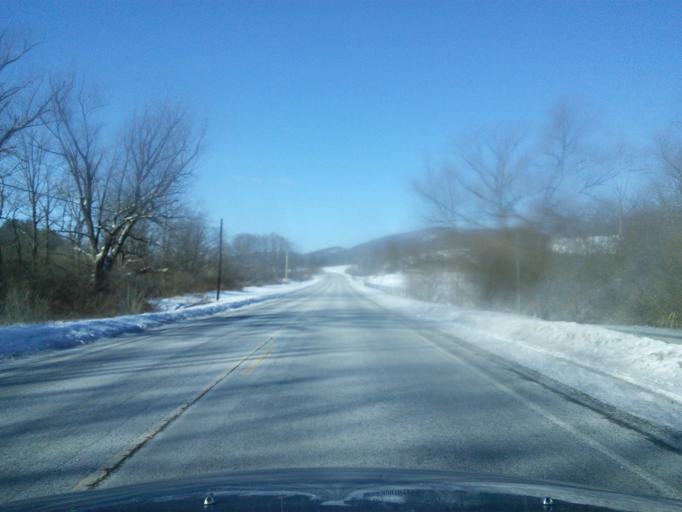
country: US
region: Pennsylvania
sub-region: Centre County
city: Park Forest Village
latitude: 40.8511
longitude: -77.8943
